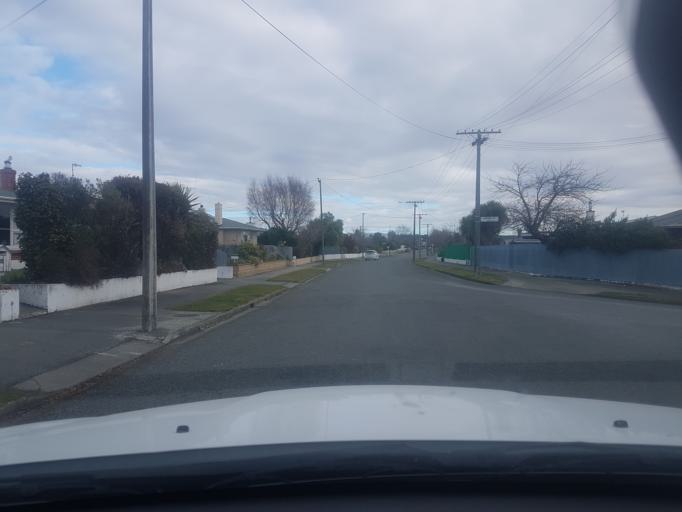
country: NZ
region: Canterbury
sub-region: Timaru District
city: Timaru
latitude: -44.3903
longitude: 171.2114
